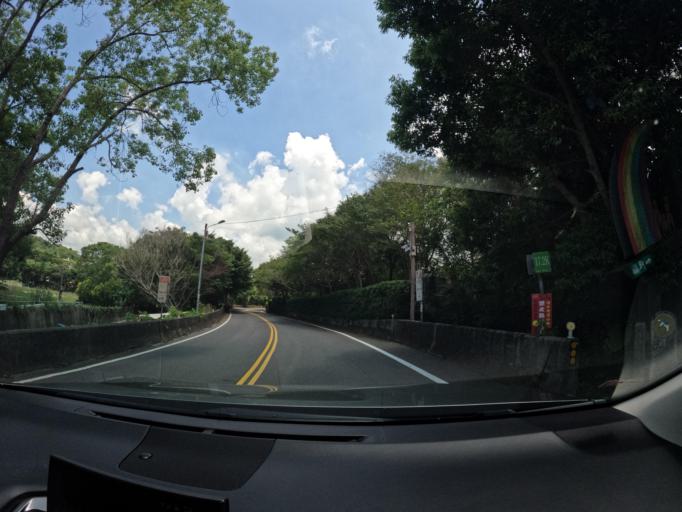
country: TW
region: Taiwan
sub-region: Miaoli
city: Miaoli
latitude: 24.4084
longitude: 120.7877
